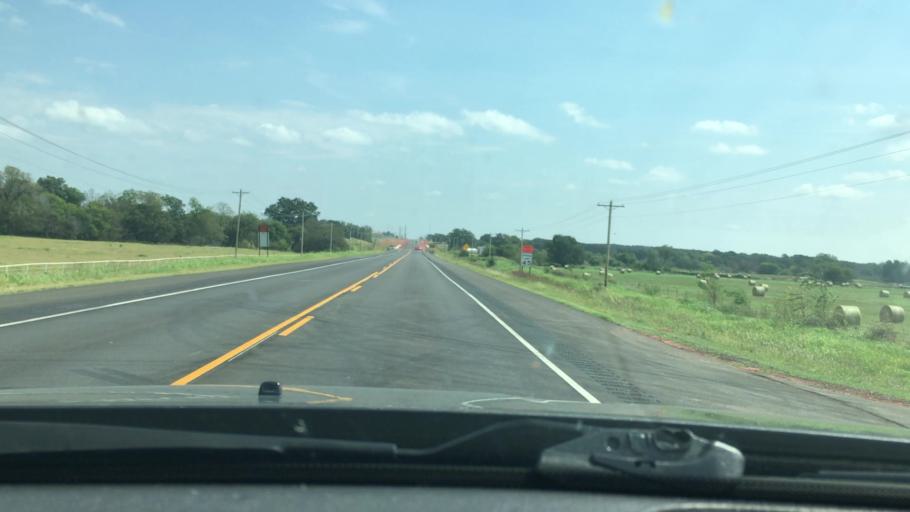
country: US
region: Oklahoma
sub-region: Cleveland County
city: Lexington
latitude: 35.0149
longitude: -97.2388
